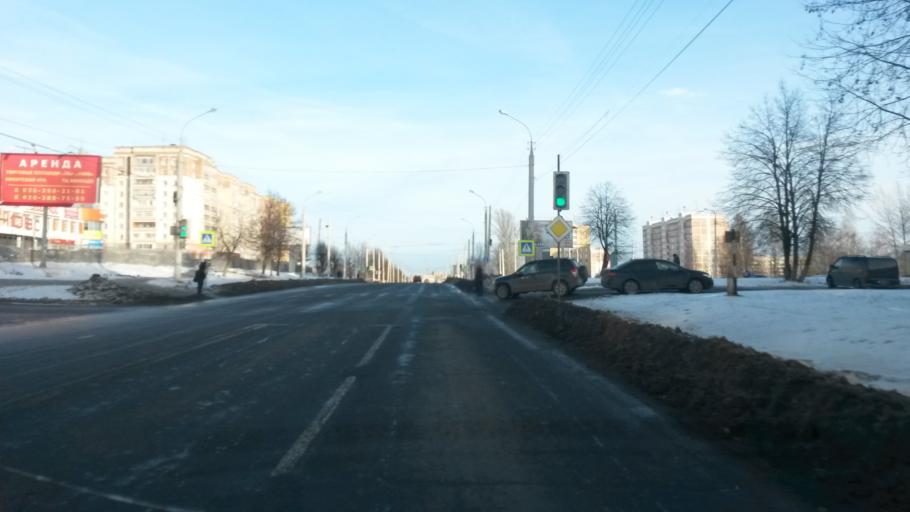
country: RU
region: Kostroma
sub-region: Kostromskoy Rayon
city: Kostroma
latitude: 57.7349
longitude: 40.9088
